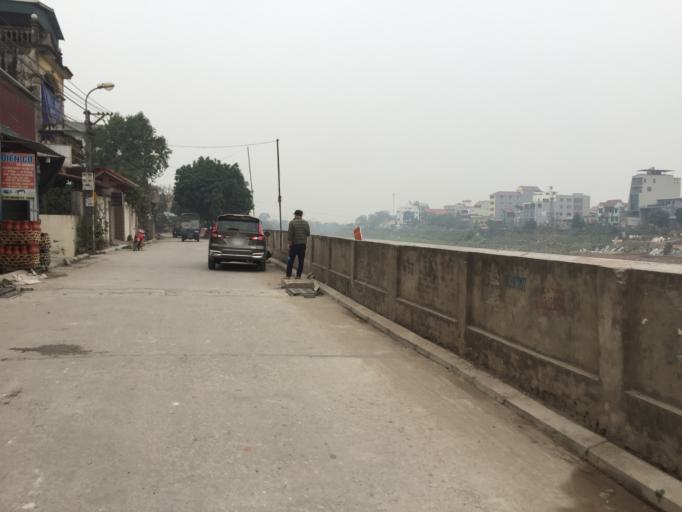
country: VN
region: Hung Yen
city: Van Giang
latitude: 20.9714
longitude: 105.9176
